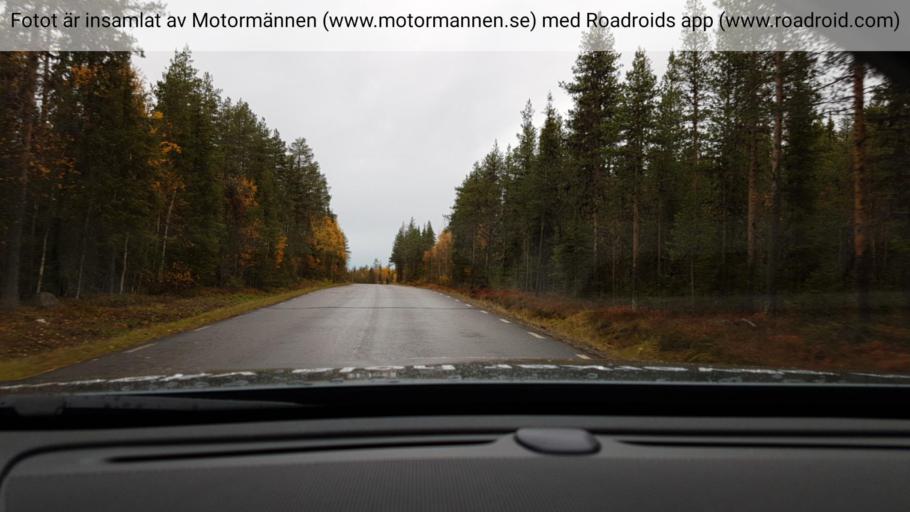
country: SE
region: Norrbotten
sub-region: Pajala Kommun
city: Pajala
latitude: 67.1628
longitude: 22.6570
